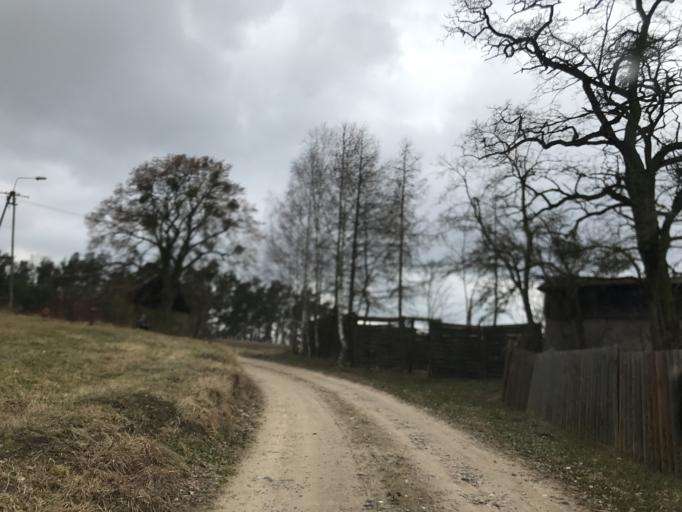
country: PL
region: Kujawsko-Pomorskie
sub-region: Powiat brodnicki
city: Gorzno
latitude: 53.2070
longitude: 19.6677
